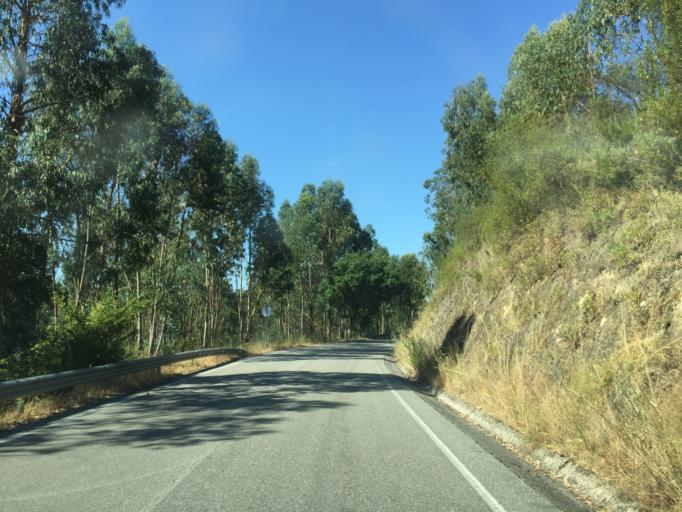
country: PT
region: Santarem
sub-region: Tomar
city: Tomar
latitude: 39.6091
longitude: -8.3395
